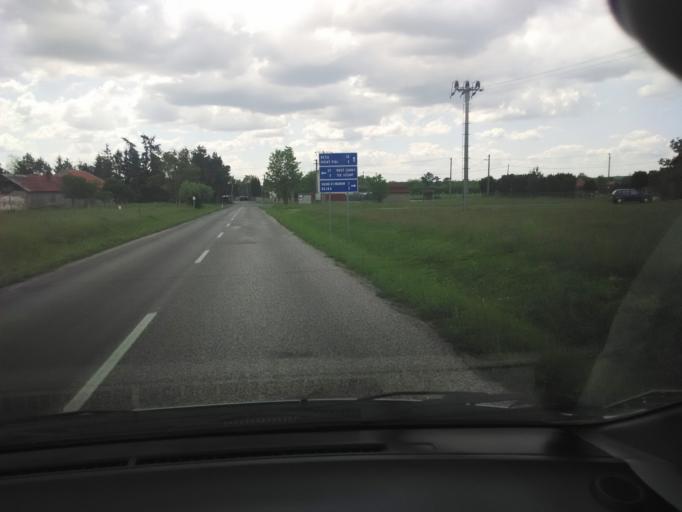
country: SK
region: Nitriansky
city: Levice
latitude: 48.1393
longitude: 18.5239
